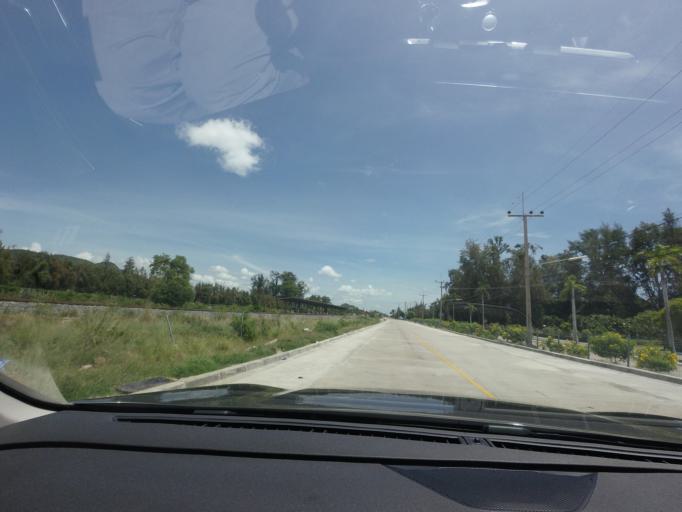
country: TH
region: Prachuap Khiri Khan
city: Hua Hin
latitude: 12.4958
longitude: 99.9728
